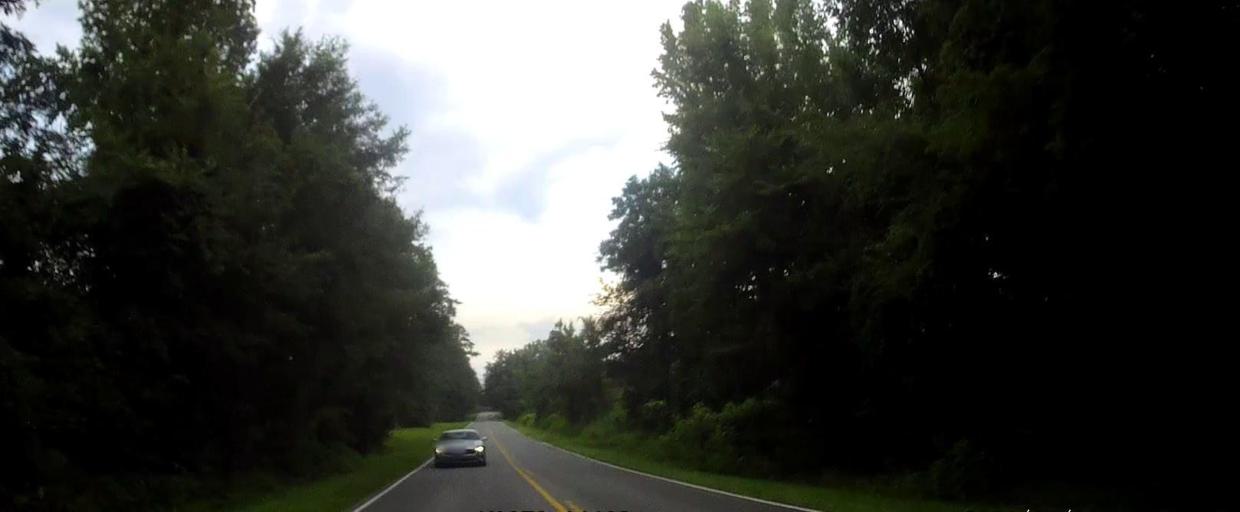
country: US
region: Georgia
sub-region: Laurens County
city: East Dublin
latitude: 32.5995
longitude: -82.8967
